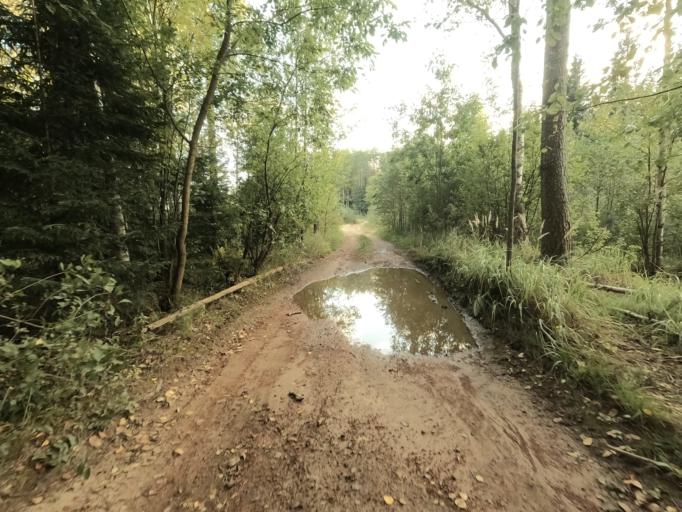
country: RU
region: Leningrad
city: Otradnoye
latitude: 59.8374
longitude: 30.7711
